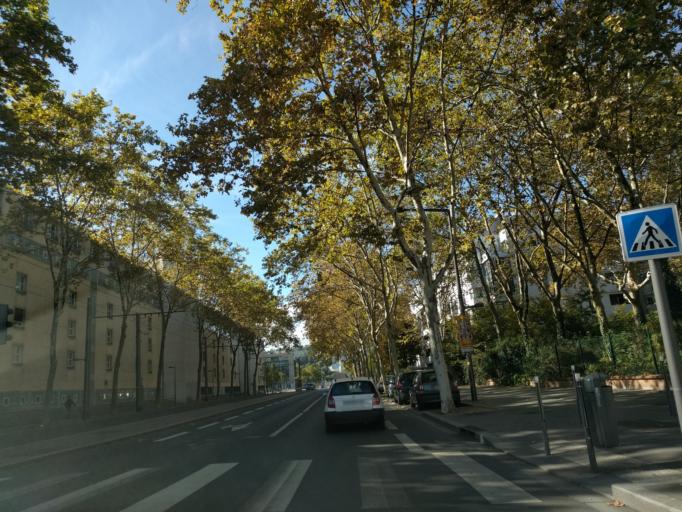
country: FR
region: Rhone-Alpes
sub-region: Departement du Rhone
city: La Mulatiere
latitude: 45.7316
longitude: 4.8279
